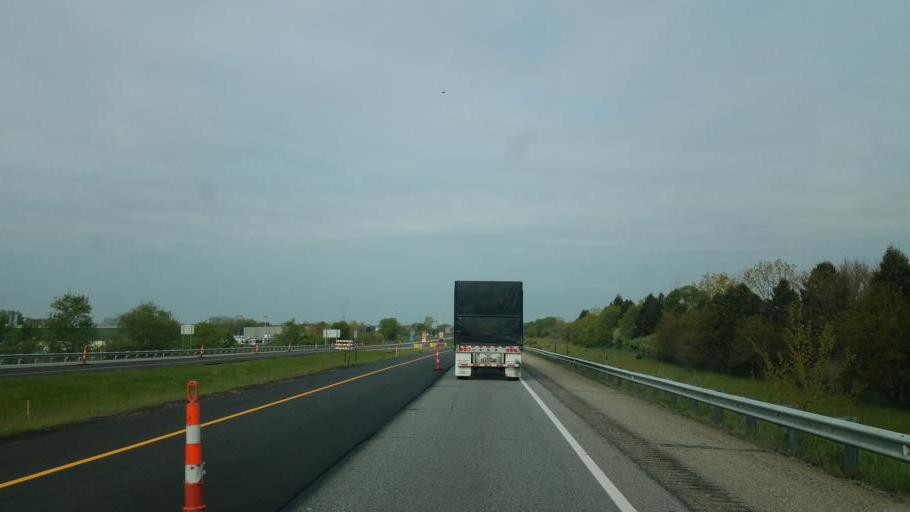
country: US
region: Indiana
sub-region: Elkhart County
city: Simonton Lake
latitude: 41.7316
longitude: -85.9889
